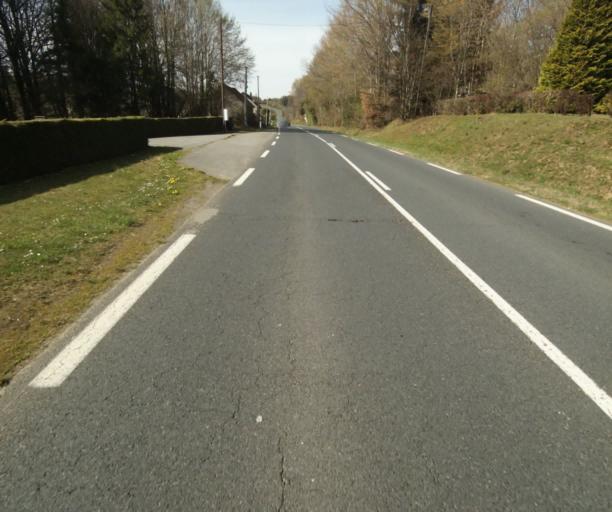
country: FR
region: Limousin
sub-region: Departement de la Correze
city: Seilhac
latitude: 45.3482
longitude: 1.7395
